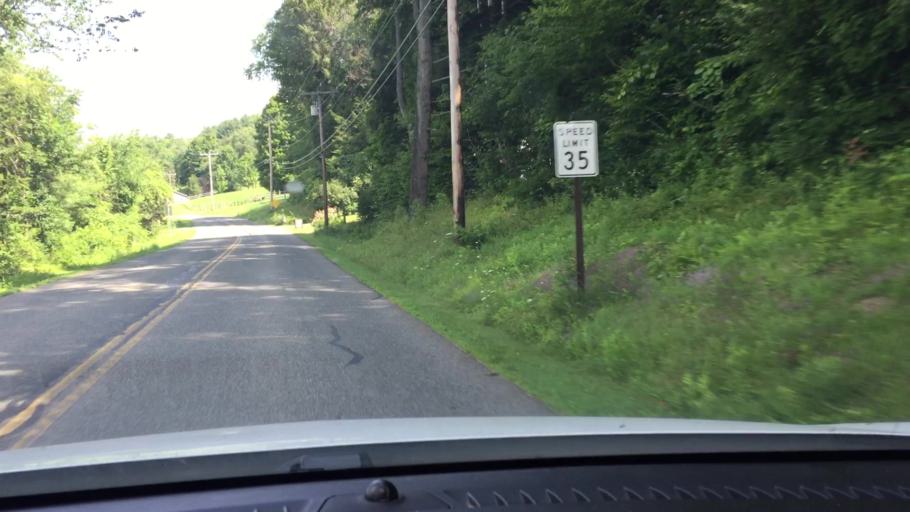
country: US
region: Massachusetts
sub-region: Berkshire County
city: Lee
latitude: 42.2371
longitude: -73.1946
